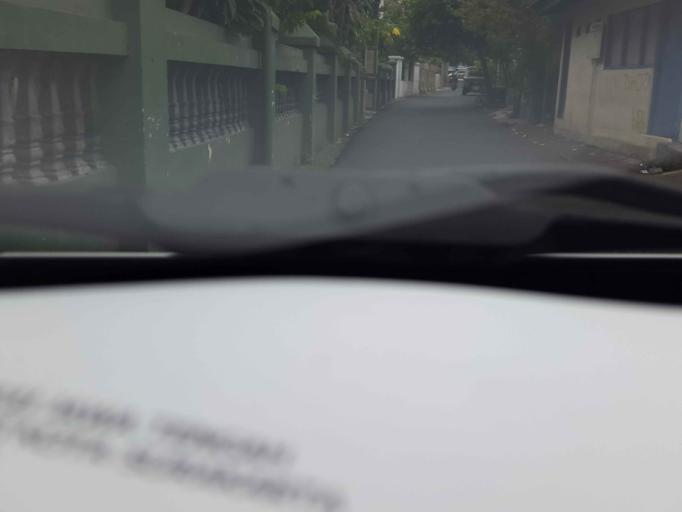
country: ID
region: Central Java
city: Surakarta
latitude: -7.5545
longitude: 110.8148
